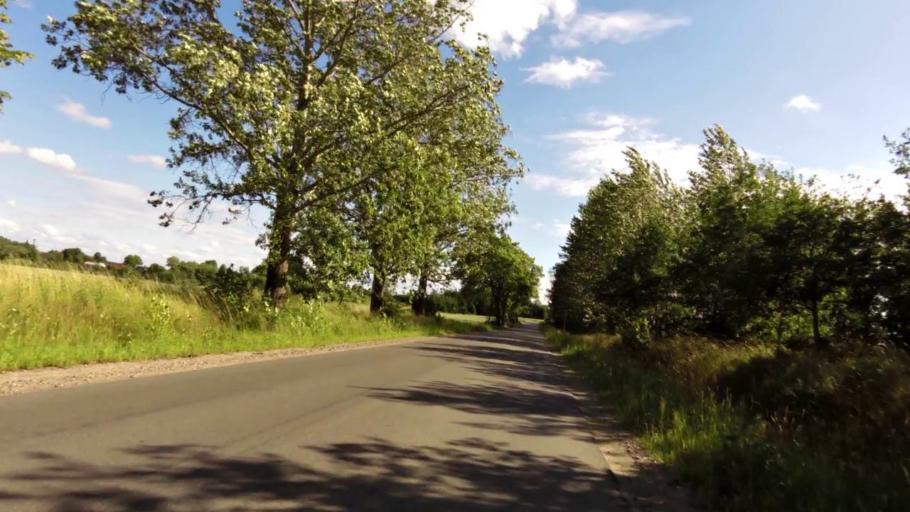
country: PL
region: West Pomeranian Voivodeship
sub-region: Powiat slawienski
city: Slawno
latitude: 54.4391
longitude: 16.7333
